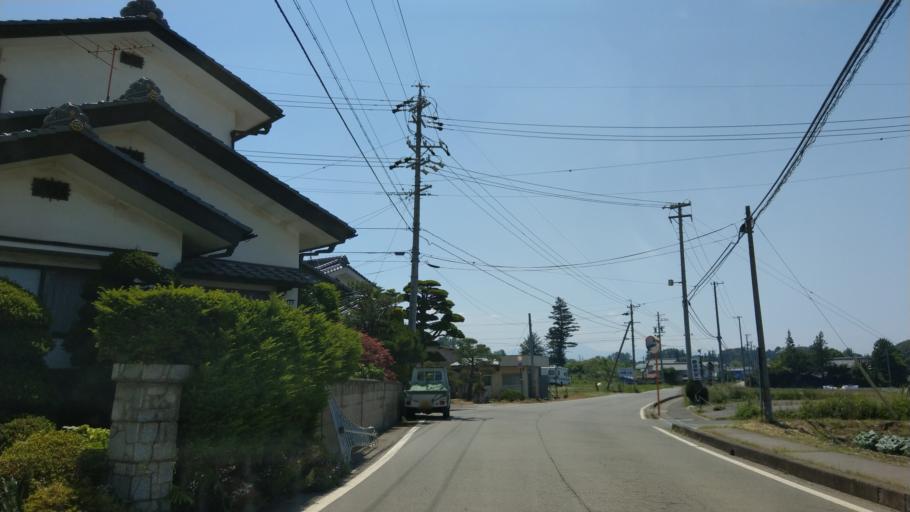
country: JP
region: Nagano
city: Komoro
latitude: 36.2896
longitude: 138.4413
